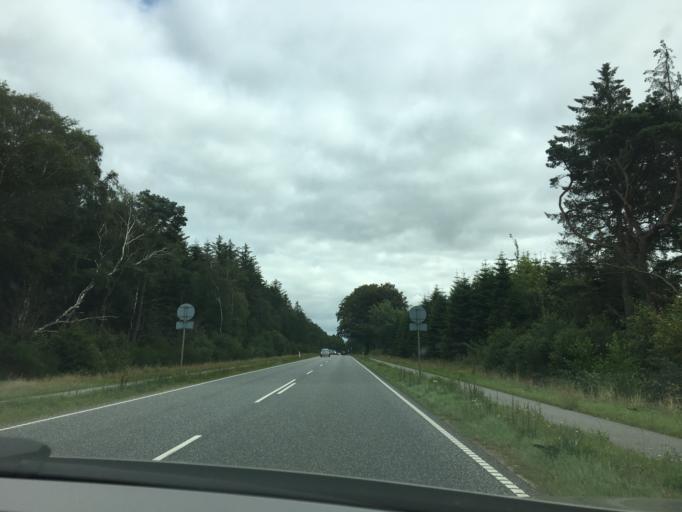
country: DK
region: Central Jutland
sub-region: Ringkobing-Skjern Kommune
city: Ringkobing
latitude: 56.0857
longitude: 8.3068
